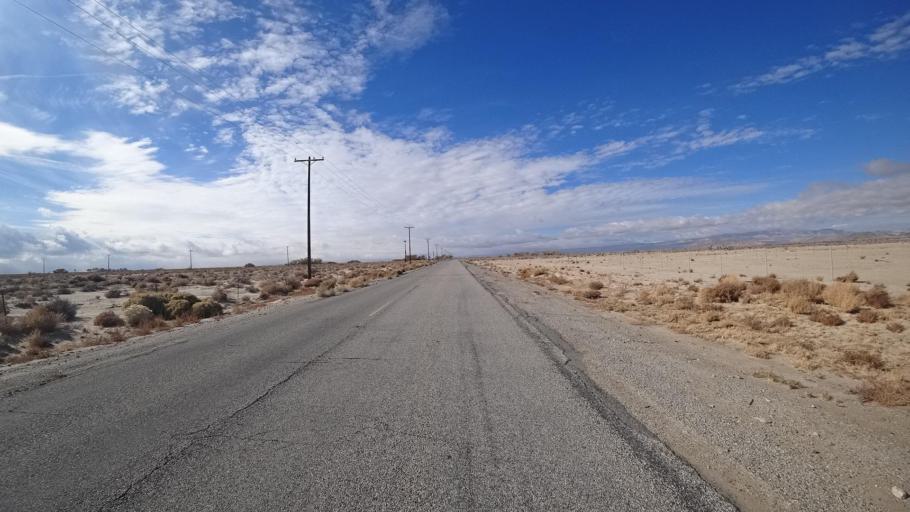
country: US
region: California
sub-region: Kern County
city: Rosamond
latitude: 34.8204
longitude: -118.1826
